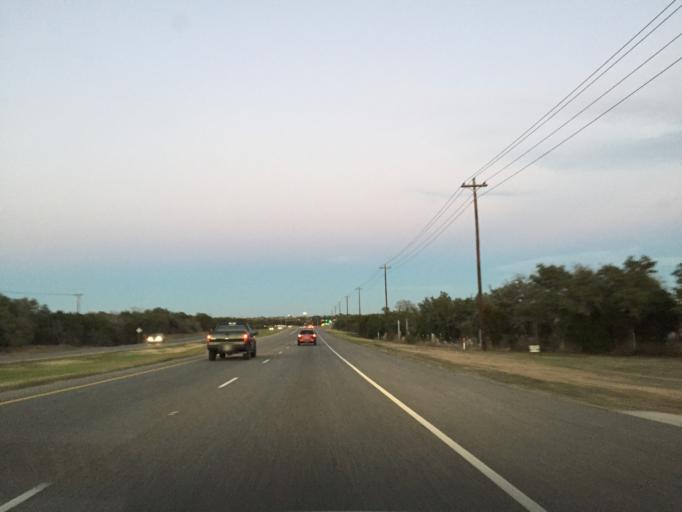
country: US
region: Texas
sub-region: Travis County
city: Jonestown
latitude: 30.5138
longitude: -97.8760
